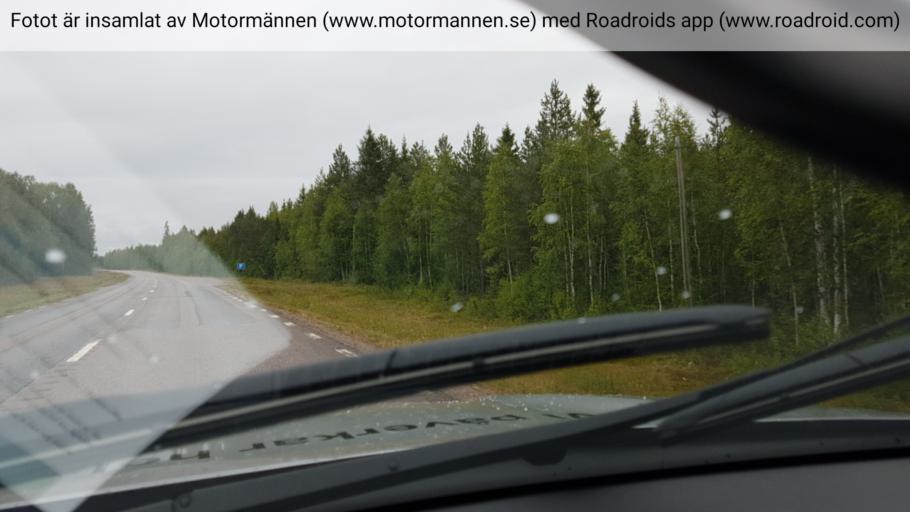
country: SE
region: Norrbotten
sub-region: Alvsbyns Kommun
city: AElvsbyn
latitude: 66.1959
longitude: 20.8830
